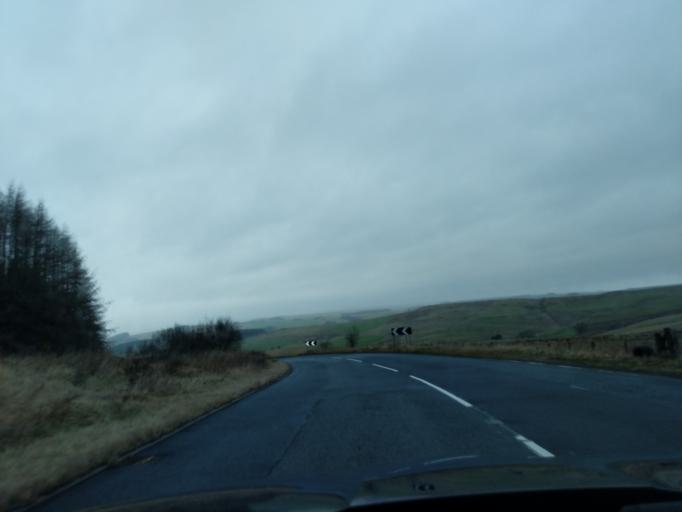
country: GB
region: England
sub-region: Northumberland
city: Otterburn
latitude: 55.2108
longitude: -2.1058
